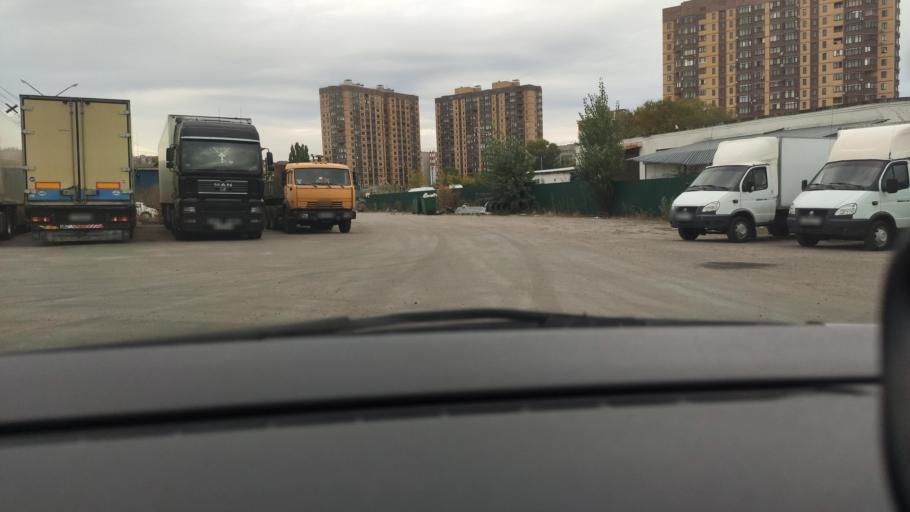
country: RU
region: Voronezj
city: Podgornoye
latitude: 51.6879
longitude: 39.1267
